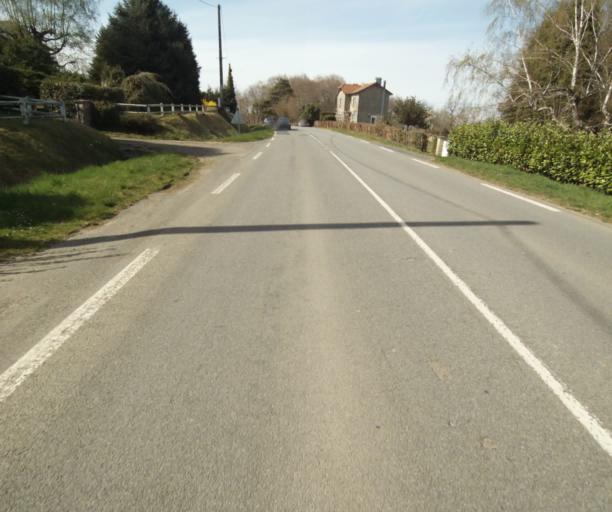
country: FR
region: Limousin
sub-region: Departement de la Correze
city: Seilhac
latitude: 45.3570
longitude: 1.7309
